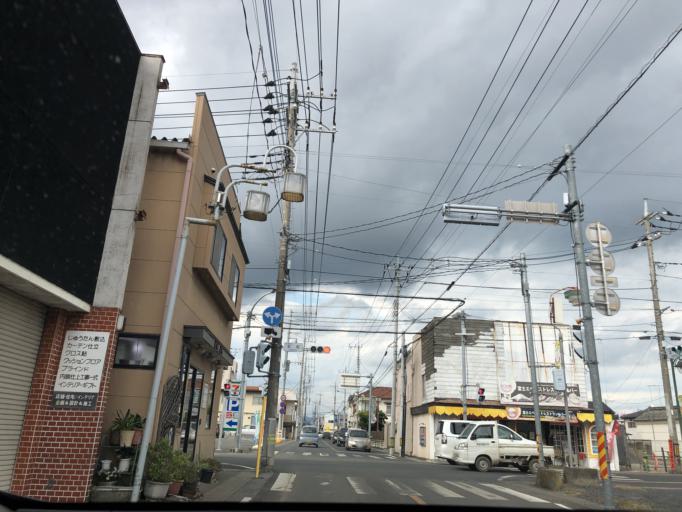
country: JP
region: Tochigi
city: Sano
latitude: 36.3133
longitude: 139.5750
